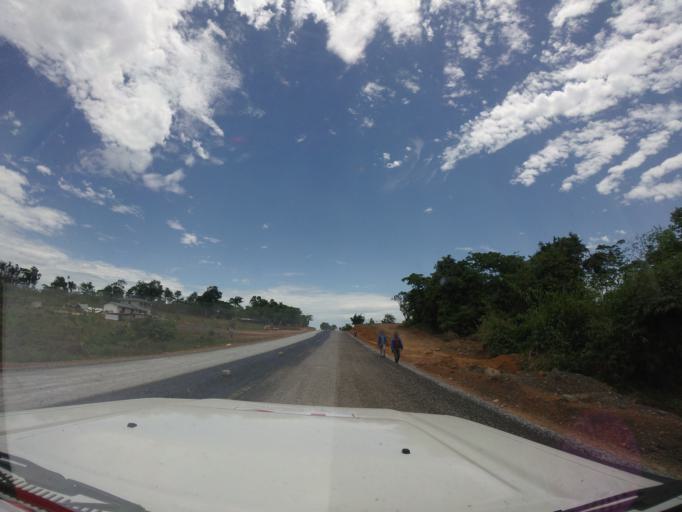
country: LR
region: Margibi
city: Kakata
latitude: 6.7499
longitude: -10.0933
